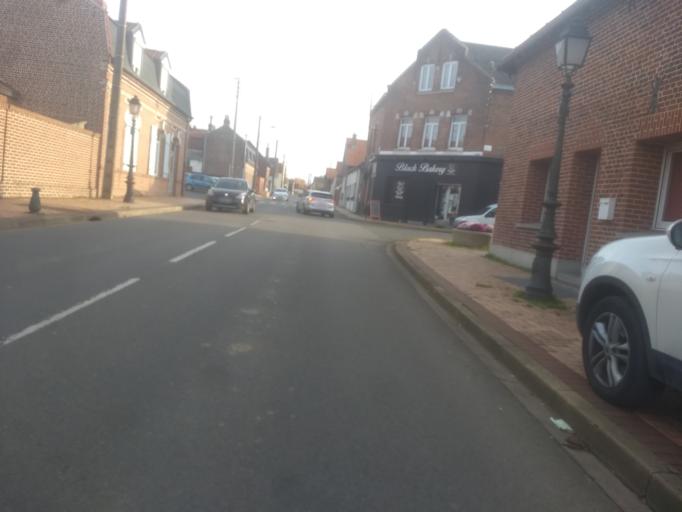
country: FR
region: Nord-Pas-de-Calais
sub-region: Departement du Pas-de-Calais
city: Agny
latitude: 50.2602
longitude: 2.7600
